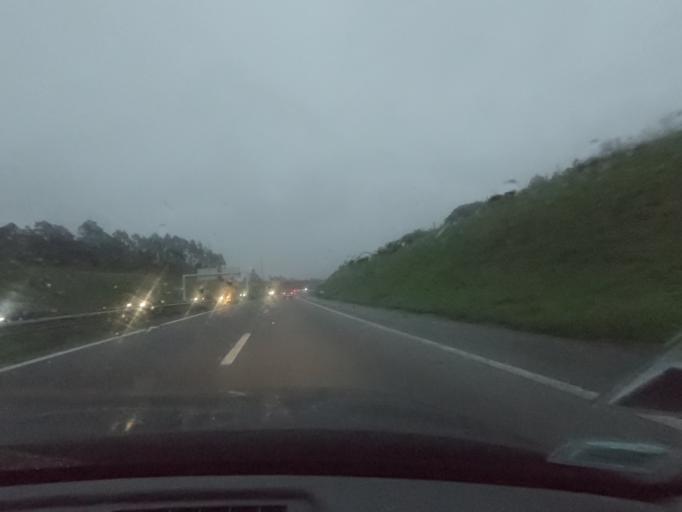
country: PT
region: Porto
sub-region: Matosinhos
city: Lavra
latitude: 41.2496
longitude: -8.6969
